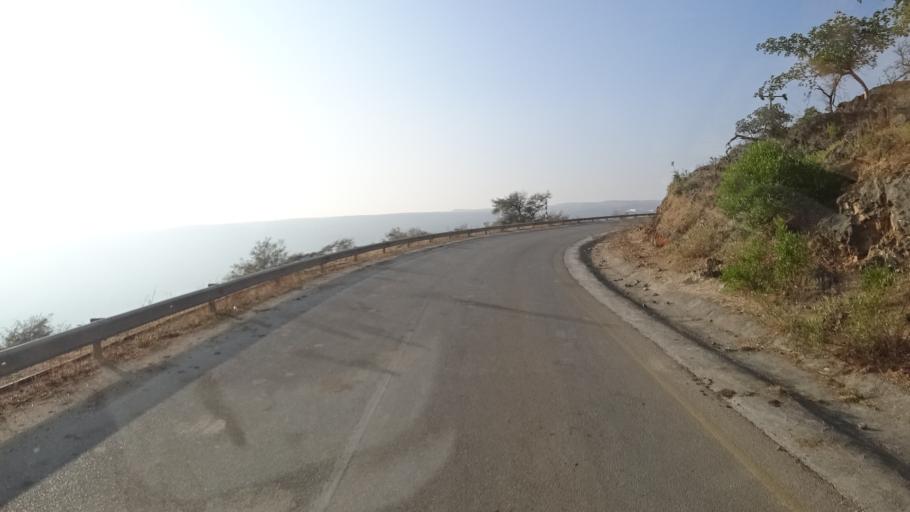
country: YE
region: Al Mahrah
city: Hawf
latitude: 16.7696
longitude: 53.3360
